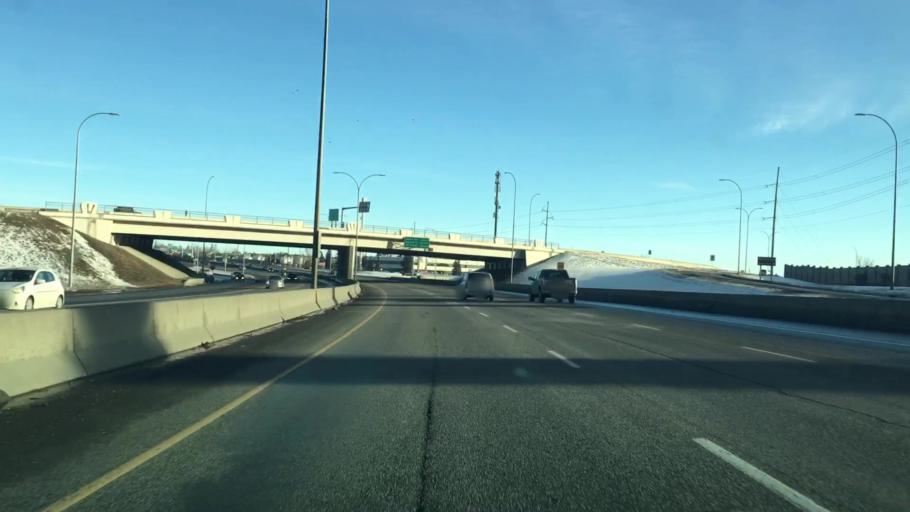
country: CA
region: Alberta
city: Calgary
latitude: 50.9814
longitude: -114.0177
